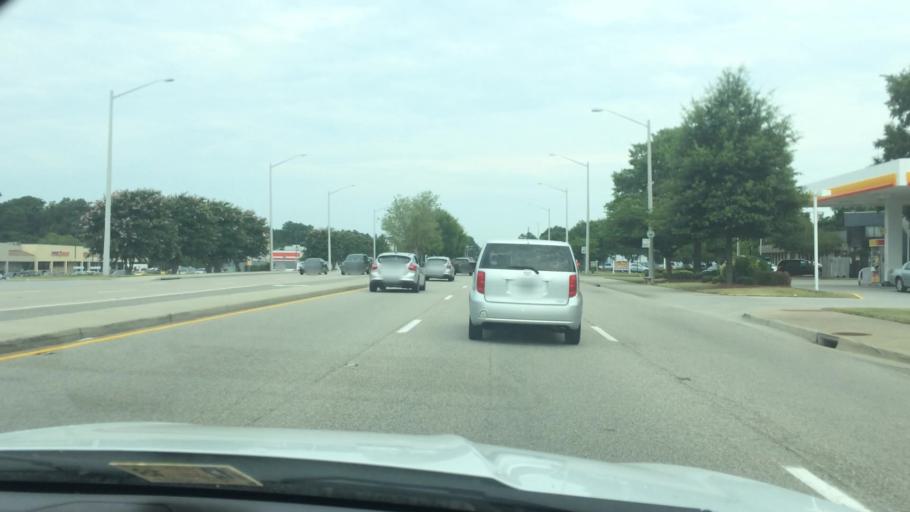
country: US
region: Virginia
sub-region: York County
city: Yorktown
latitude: 37.1493
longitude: -76.5283
